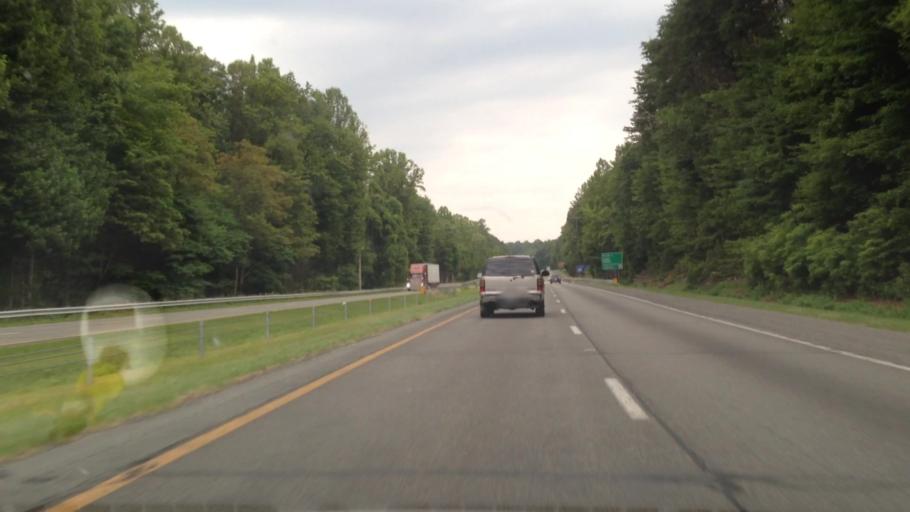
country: US
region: North Carolina
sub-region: Surry County
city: Pilot Mountain
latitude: 36.3267
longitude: -80.4503
